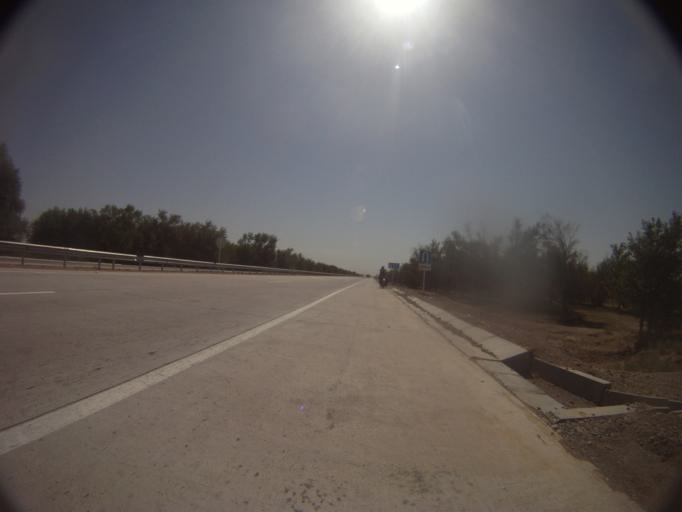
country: KZ
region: Ongtustik Qazaqstan
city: Bayaldyr
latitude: 43.1008
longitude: 68.6278
